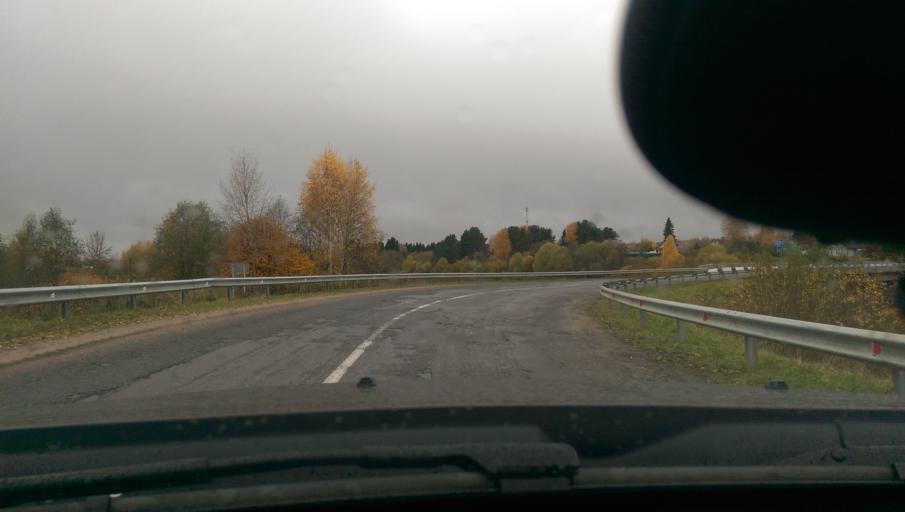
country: RU
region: Jaroslavl
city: Poshekhon'ye
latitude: 58.5160
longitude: 39.1239
